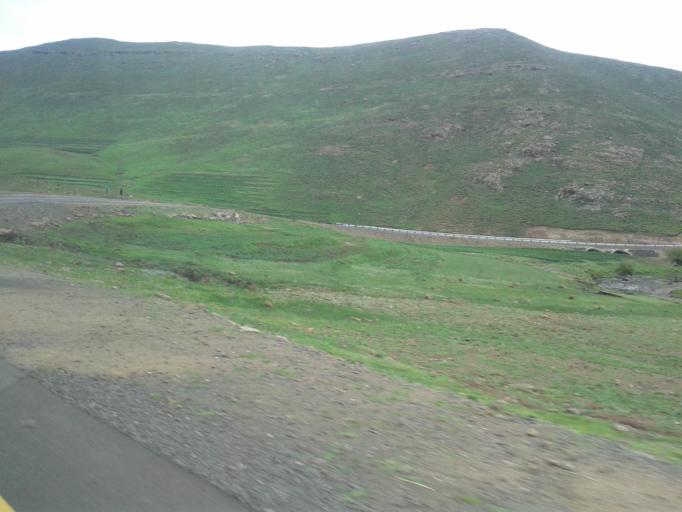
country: LS
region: Maseru
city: Nako
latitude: -29.8080
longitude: 28.0275
